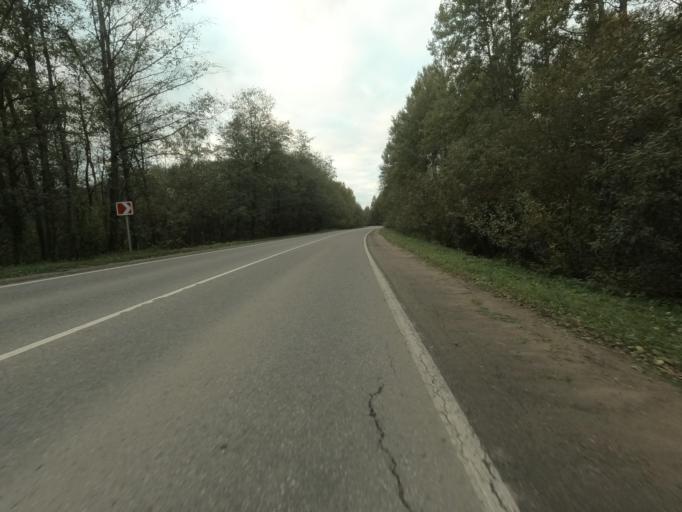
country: RU
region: Leningrad
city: Pavlovo
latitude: 59.8031
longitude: 30.9363
